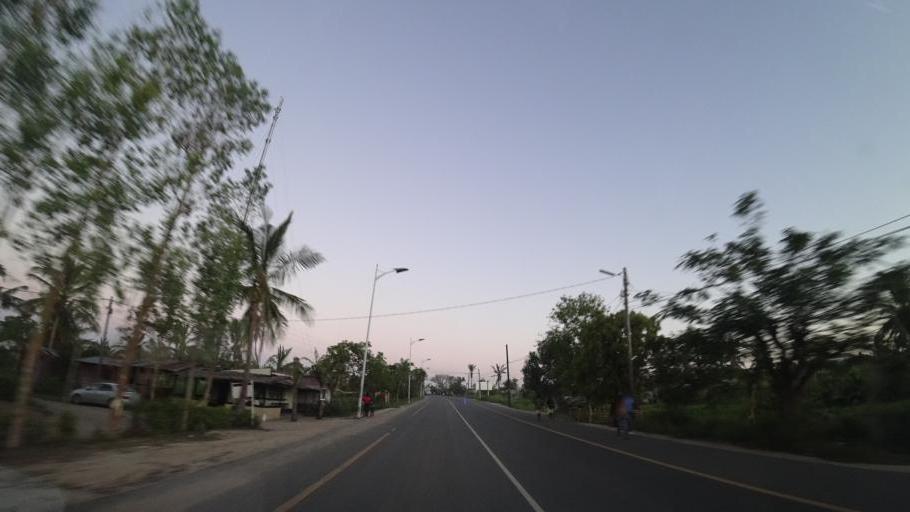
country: MZ
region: Sofala
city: Dondo
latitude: -19.5313
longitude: 34.6289
